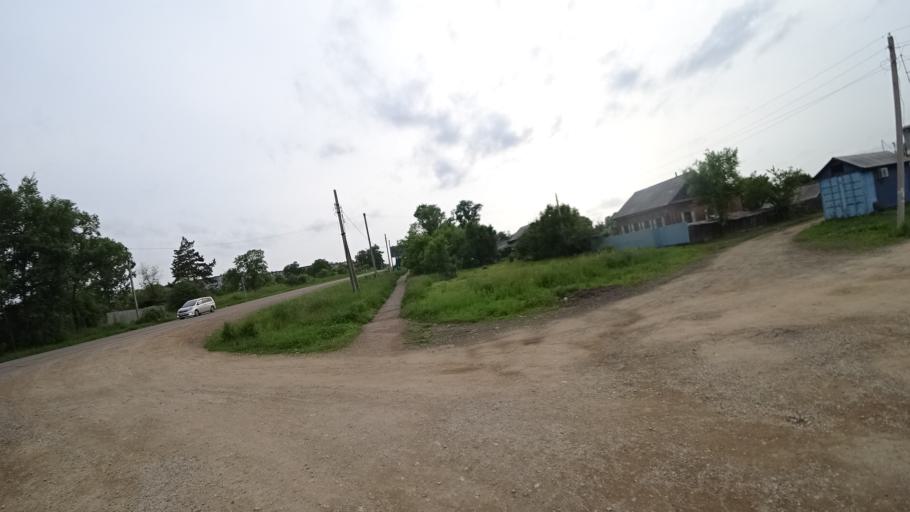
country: RU
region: Primorskiy
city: Novosysoyevka
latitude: 44.2301
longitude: 133.3647
